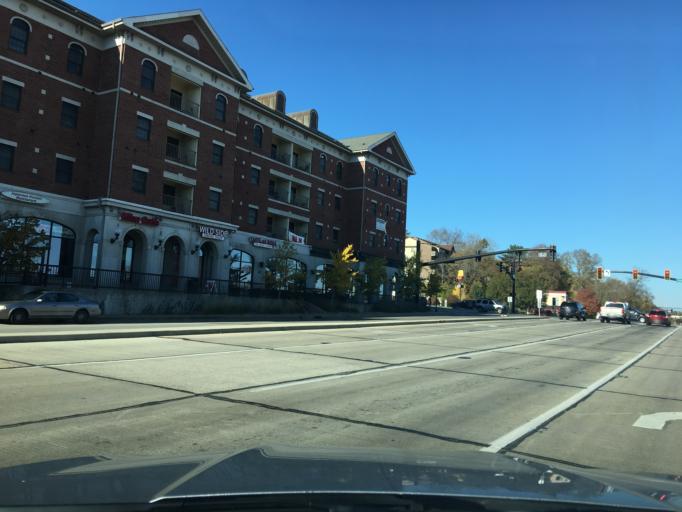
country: US
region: Indiana
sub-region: Tippecanoe County
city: West Lafayette
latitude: 40.4214
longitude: -86.9046
